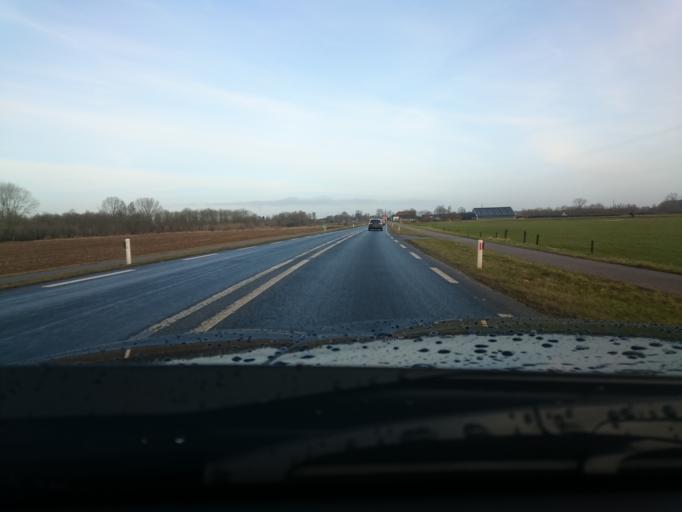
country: NL
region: Gelderland
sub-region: Gemeente Voorst
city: Voorst
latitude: 52.1492
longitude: 6.1490
